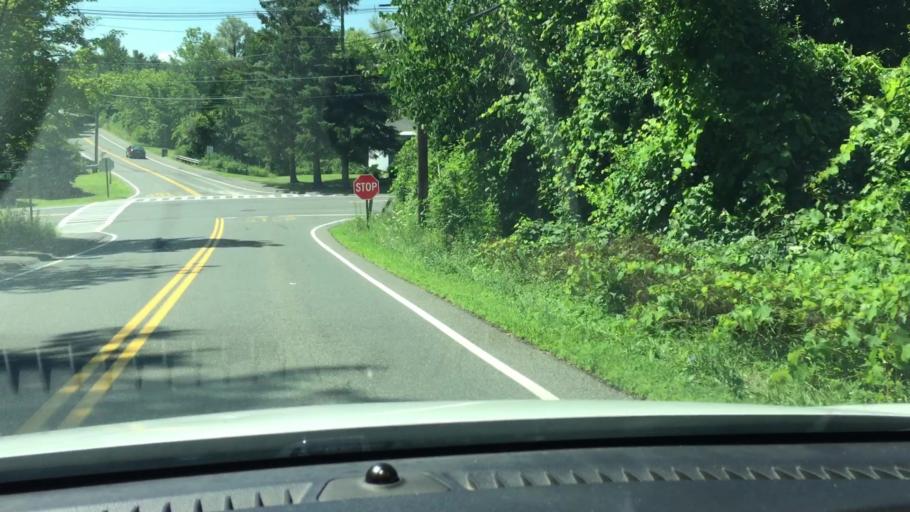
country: US
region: Massachusetts
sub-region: Berkshire County
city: Lenox
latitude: 42.3561
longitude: -73.2595
